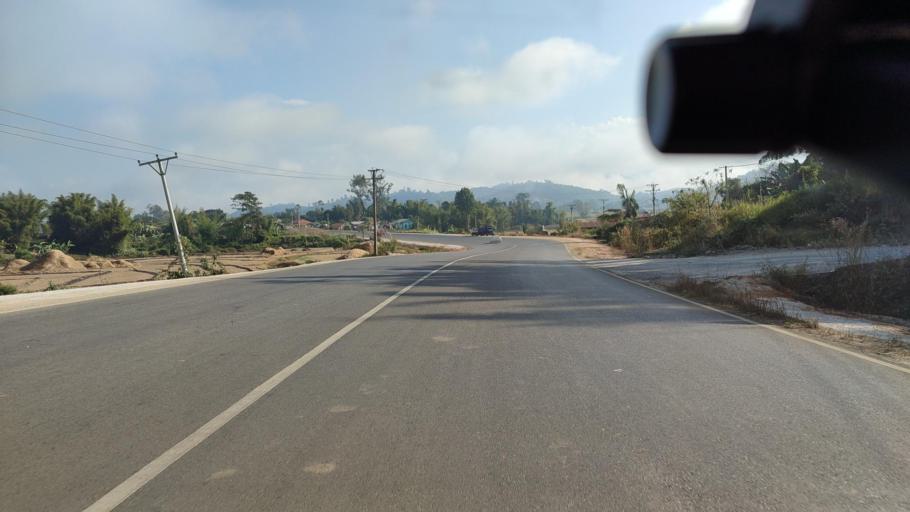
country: MM
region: Shan
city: Lashio
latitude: 23.1946
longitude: 97.8921
